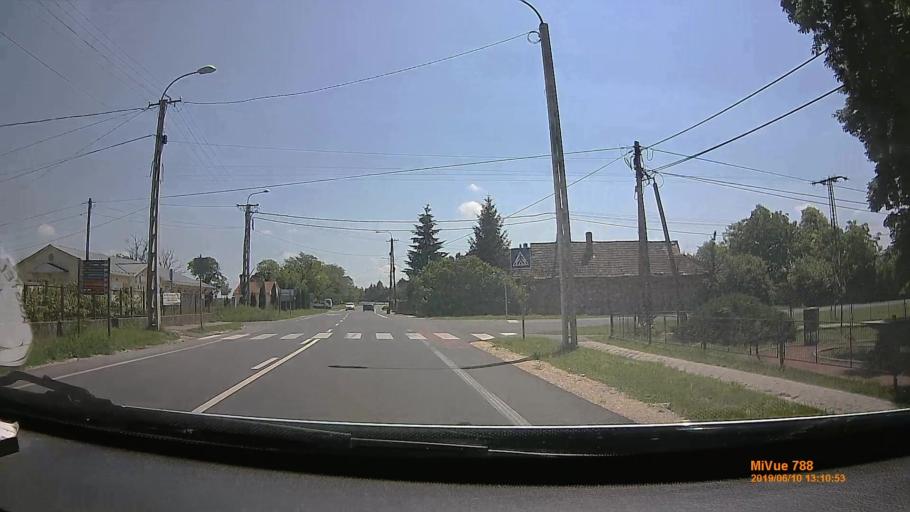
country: HU
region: Borsod-Abauj-Zemplen
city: Hernadnemeti
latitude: 48.0733
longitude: 20.9786
